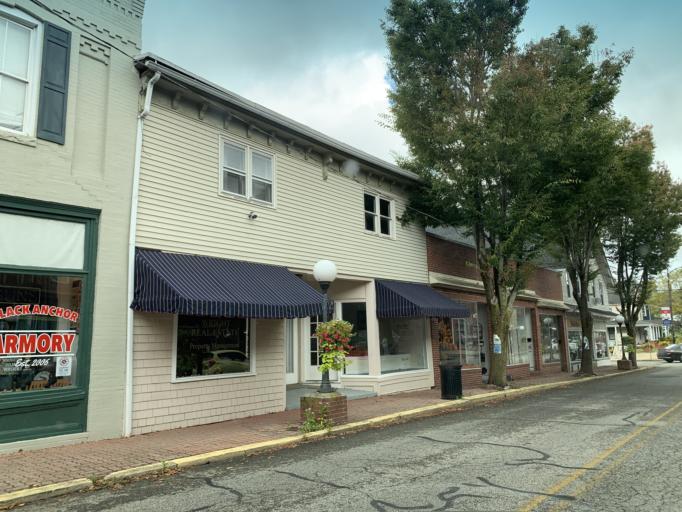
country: US
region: Maryland
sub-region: Caroline County
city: Denton
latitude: 38.8862
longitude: -75.8322
